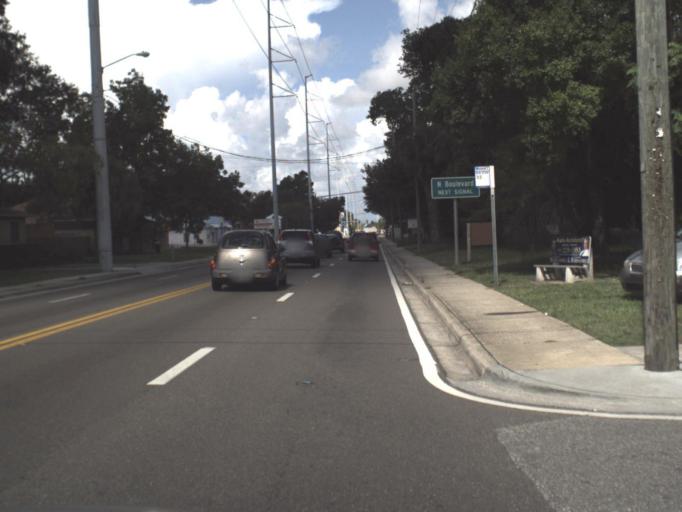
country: US
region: Florida
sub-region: Hillsborough County
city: Tampa
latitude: 27.9816
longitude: -82.4635
